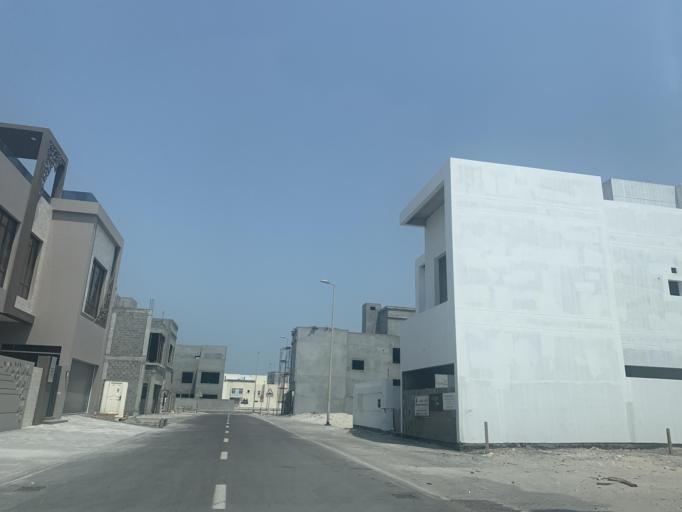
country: BH
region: Muharraq
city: Al Hadd
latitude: 26.2407
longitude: 50.6620
